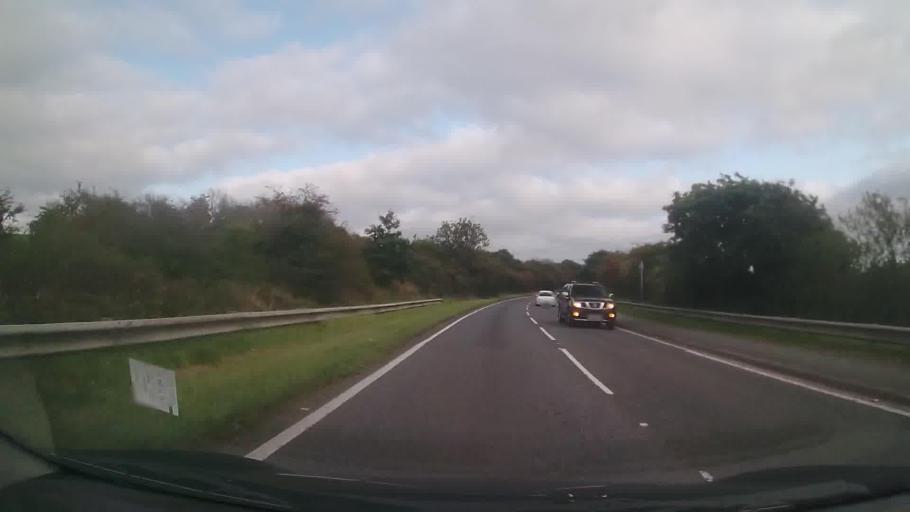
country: GB
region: Wales
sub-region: Pembrokeshire
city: Neyland
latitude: 51.7158
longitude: -4.9416
